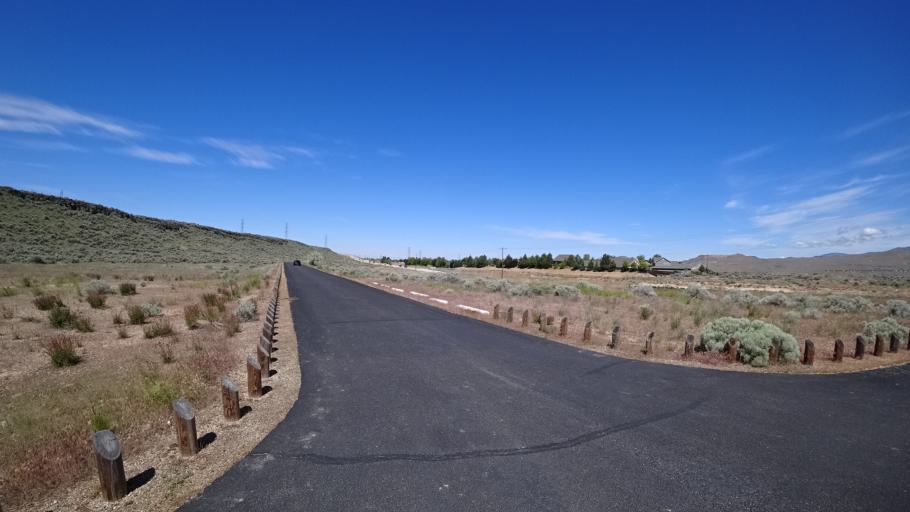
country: US
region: Idaho
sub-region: Ada County
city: Boise
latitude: 43.5423
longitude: -116.1107
